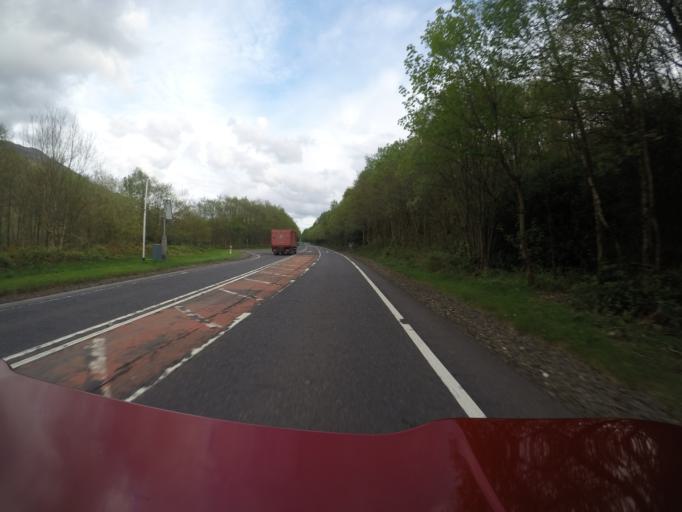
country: GB
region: Scotland
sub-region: Argyll and Bute
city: Garelochhead
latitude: 56.1861
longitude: -4.6971
